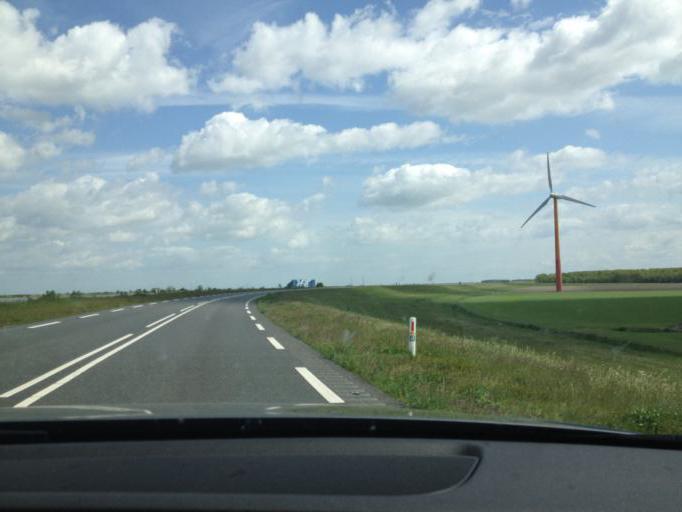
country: NL
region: North Holland
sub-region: Gemeente Waterland
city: Marken
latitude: 52.3796
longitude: 5.1235
